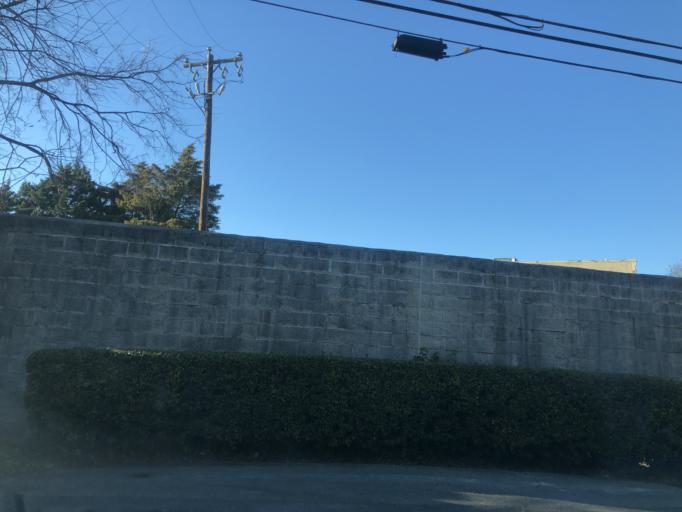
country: US
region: Texas
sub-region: Travis County
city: Windemere
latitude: 30.4813
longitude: -97.6576
